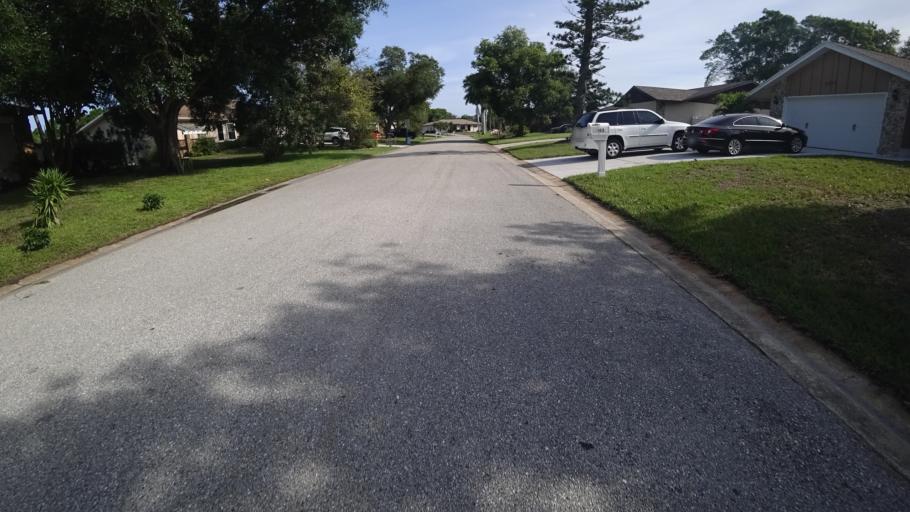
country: US
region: Florida
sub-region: Manatee County
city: West Bradenton
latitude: 27.5093
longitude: -82.6390
